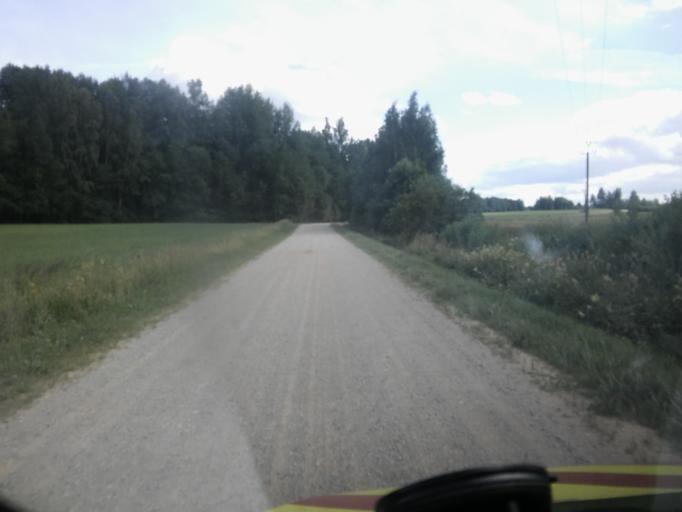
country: EE
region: Viljandimaa
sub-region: Karksi vald
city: Karksi-Nuia
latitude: 58.0795
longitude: 25.5182
